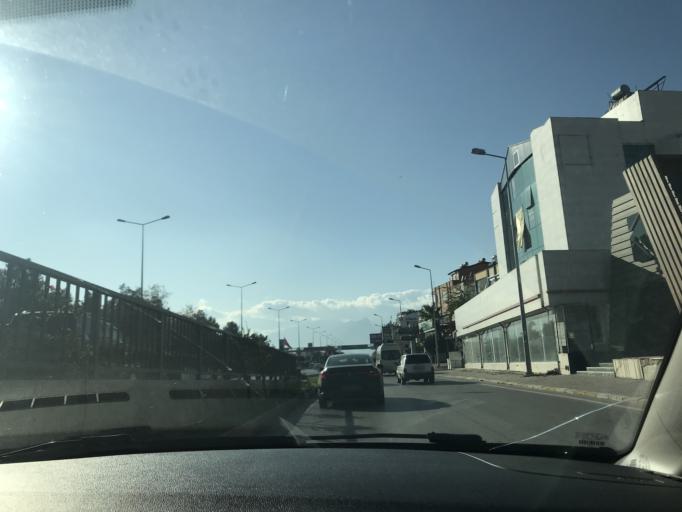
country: TR
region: Antalya
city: Antalya
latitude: 36.9103
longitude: 30.6950
